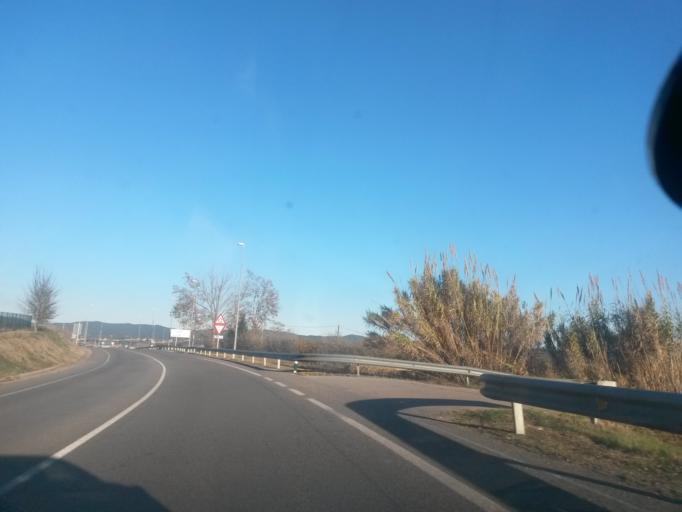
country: ES
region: Catalonia
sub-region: Provincia de Girona
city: Aiguaviva
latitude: 41.9382
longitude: 2.7806
